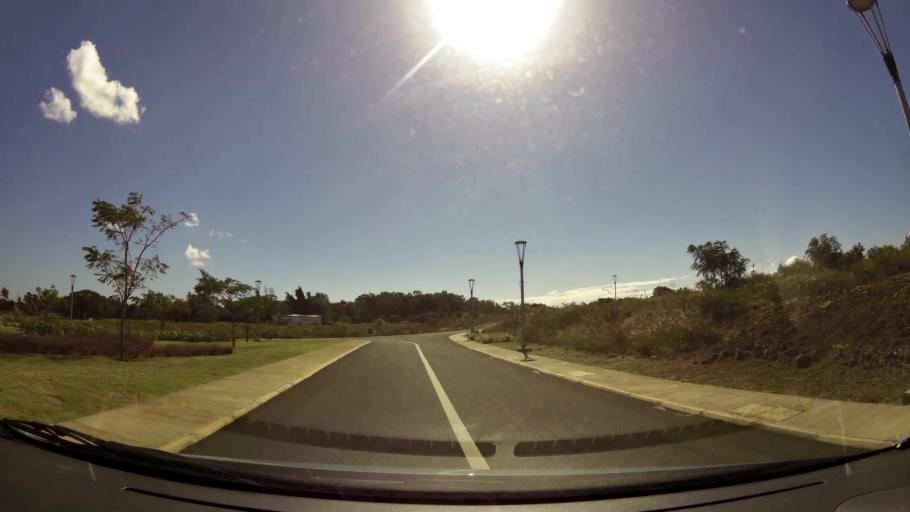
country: MU
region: Black River
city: Flic en Flac
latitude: -20.2692
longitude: 57.3858
